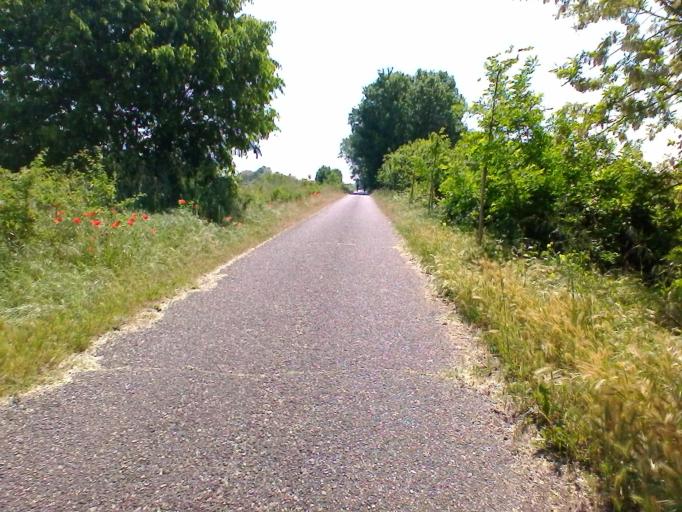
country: IT
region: Lombardy
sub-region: Provincia di Mantova
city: Soave
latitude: 45.1904
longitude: 10.7285
